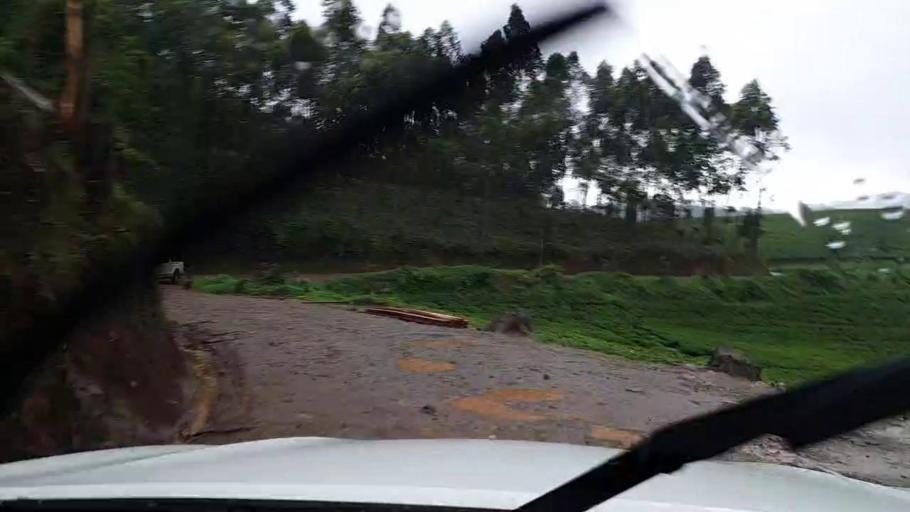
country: RW
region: Western Province
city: Cyangugu
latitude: -2.4627
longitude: 29.0354
